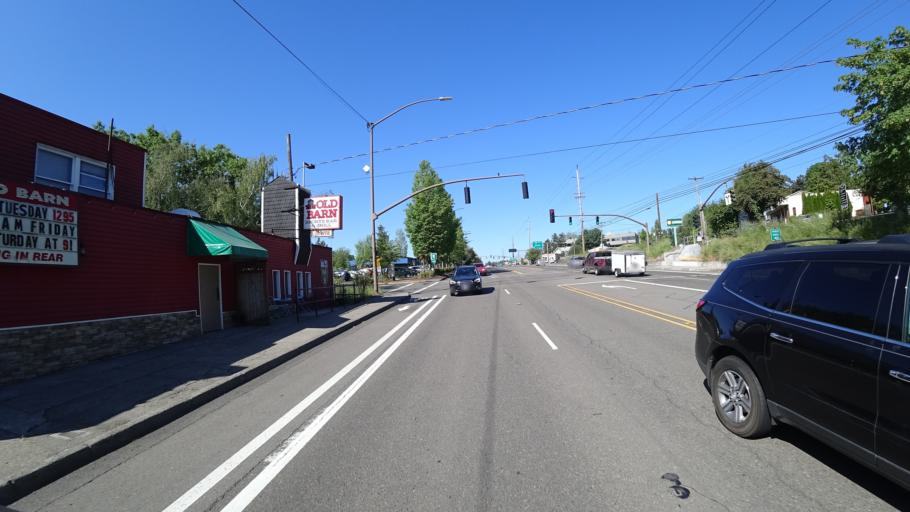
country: US
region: Oregon
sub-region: Washington County
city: Garden Home-Whitford
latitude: 45.4554
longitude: -122.7164
